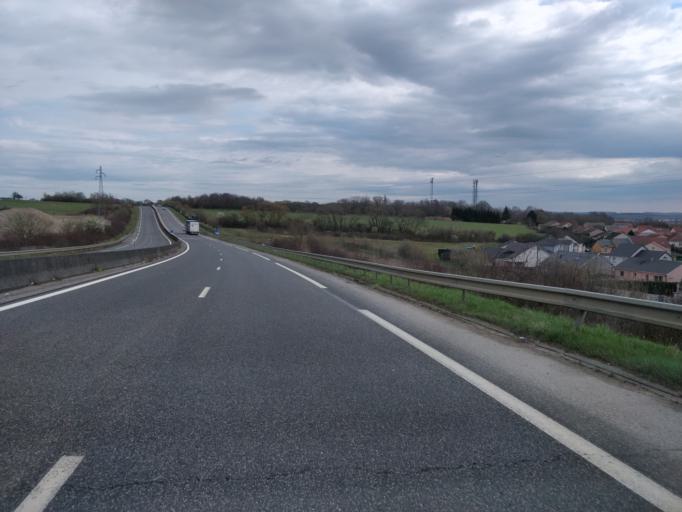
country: FR
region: Lorraine
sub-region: Departement de la Moselle
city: Gandrange
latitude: 49.2757
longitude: 6.1182
